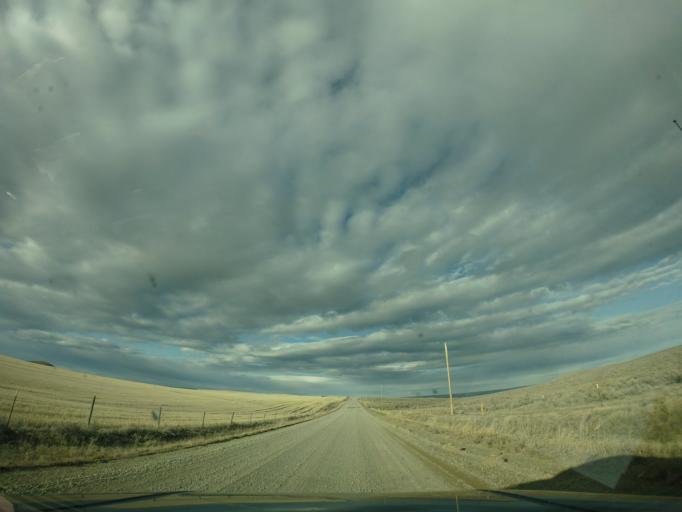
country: US
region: Montana
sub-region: Yellowstone County
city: Laurel
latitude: 45.9015
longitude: -108.8809
